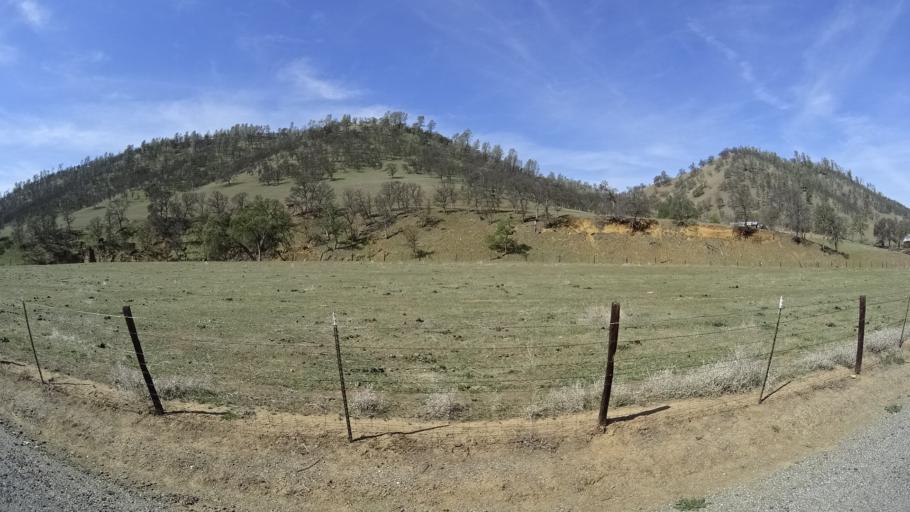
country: US
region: California
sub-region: Glenn County
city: Willows
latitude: 39.5051
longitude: -122.4533
